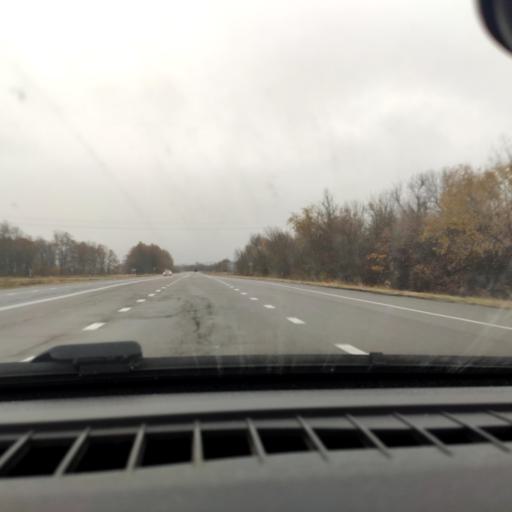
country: RU
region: Voronezj
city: Kolodeznyy
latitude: 51.3197
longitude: 39.0276
